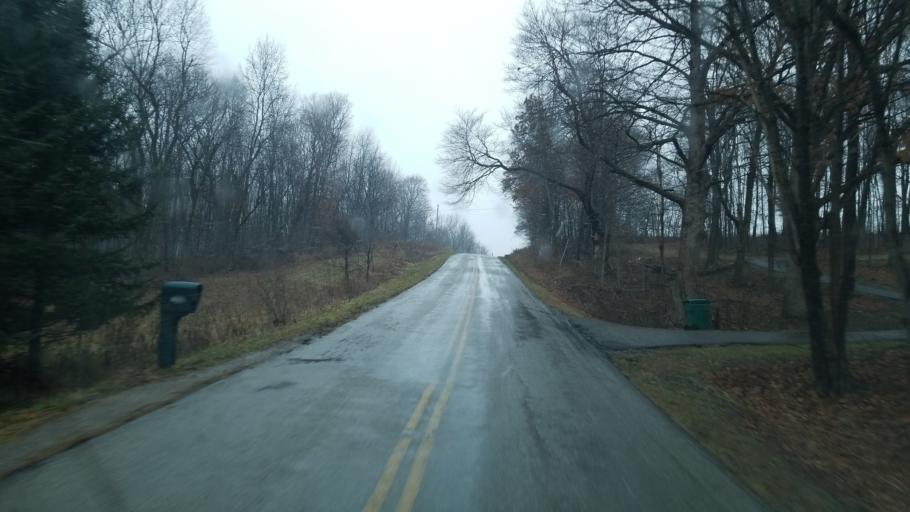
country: US
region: Ohio
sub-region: Licking County
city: Utica
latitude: 40.2195
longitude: -82.3370
